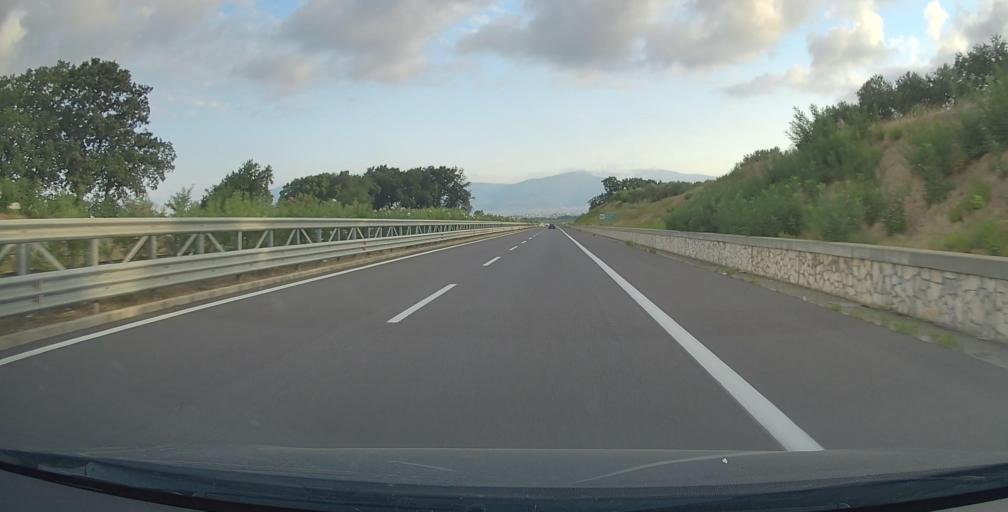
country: IT
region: Calabria
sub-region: Provincia di Catanzaro
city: Acconia
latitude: 38.8731
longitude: 16.2815
